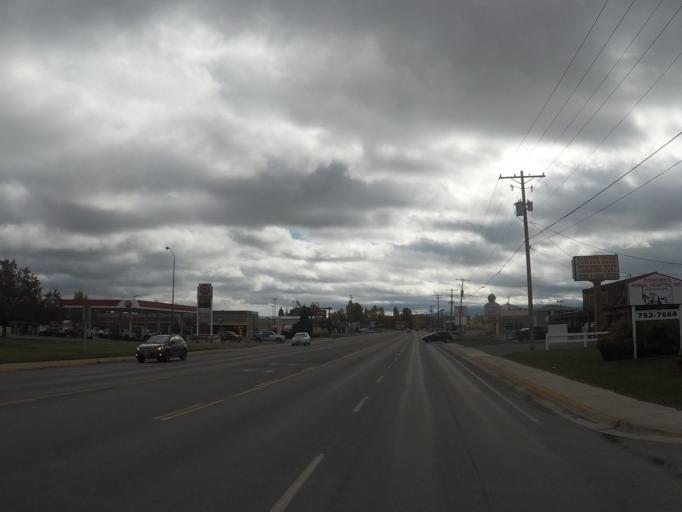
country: US
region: Montana
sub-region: Flathead County
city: Evergreen
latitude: 48.2188
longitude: -114.2774
